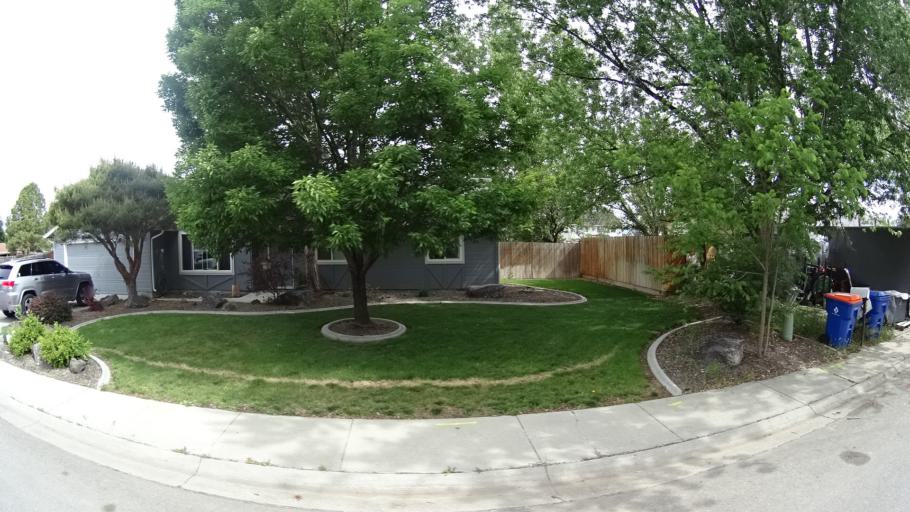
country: US
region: Idaho
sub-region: Ada County
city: Garden City
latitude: 43.5387
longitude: -116.3090
